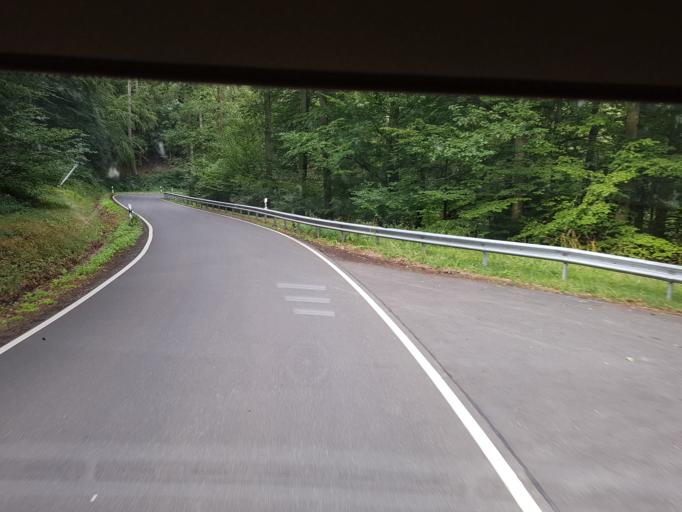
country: DE
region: Rheinland-Pfalz
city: Senheim
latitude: 50.0860
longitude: 7.2282
